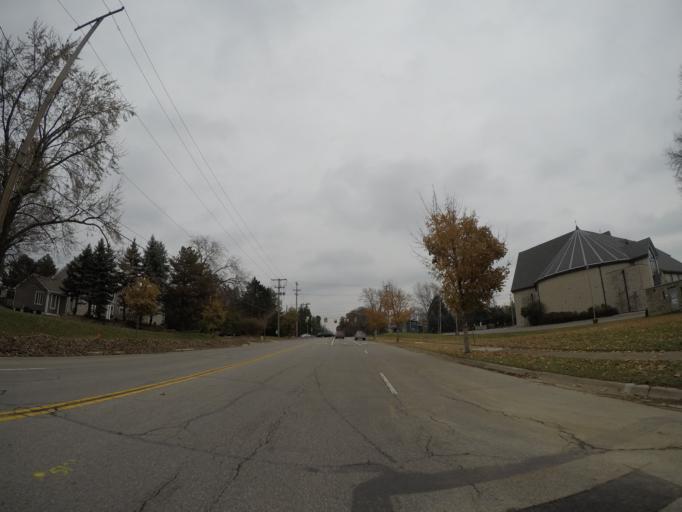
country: US
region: Ohio
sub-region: Franklin County
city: Upper Arlington
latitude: 40.0406
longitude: -83.0679
